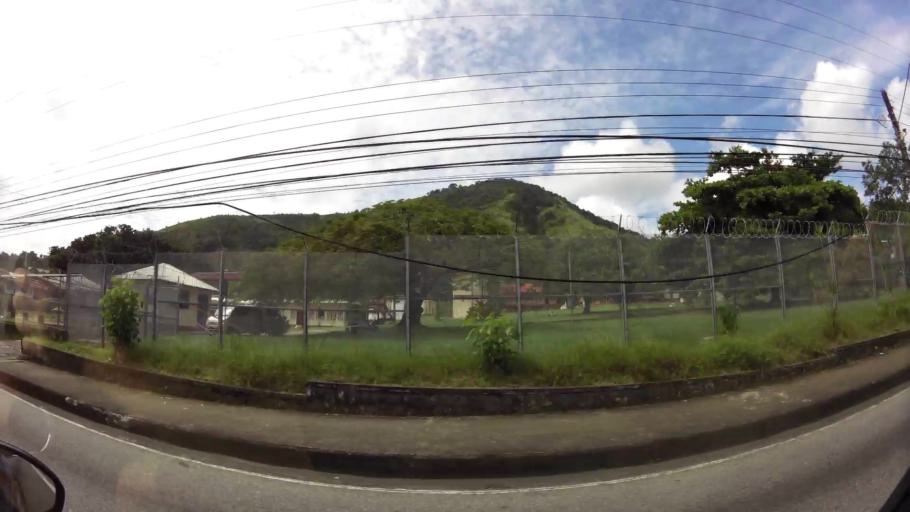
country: TT
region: Diego Martin
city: Petit Valley
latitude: 10.7042
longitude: -61.5558
